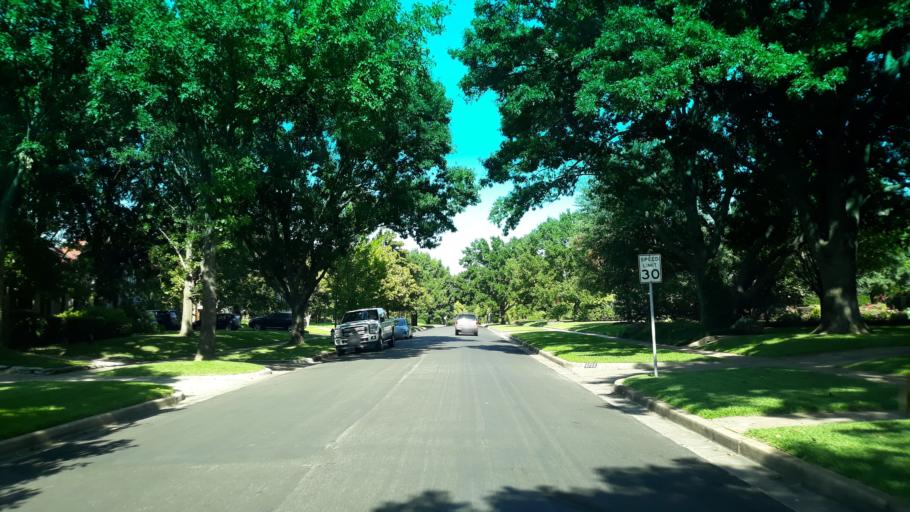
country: US
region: Texas
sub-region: Dallas County
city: Highland Park
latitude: 32.8193
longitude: -96.7458
